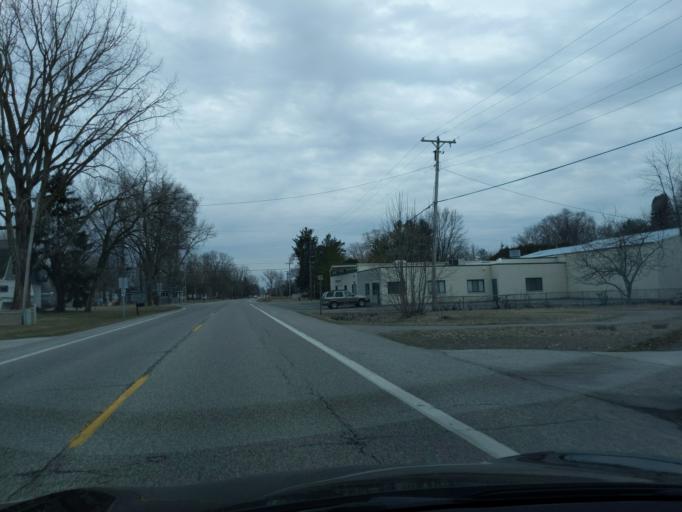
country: US
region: Michigan
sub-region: Bay County
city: Bay City
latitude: 43.6536
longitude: -83.9125
